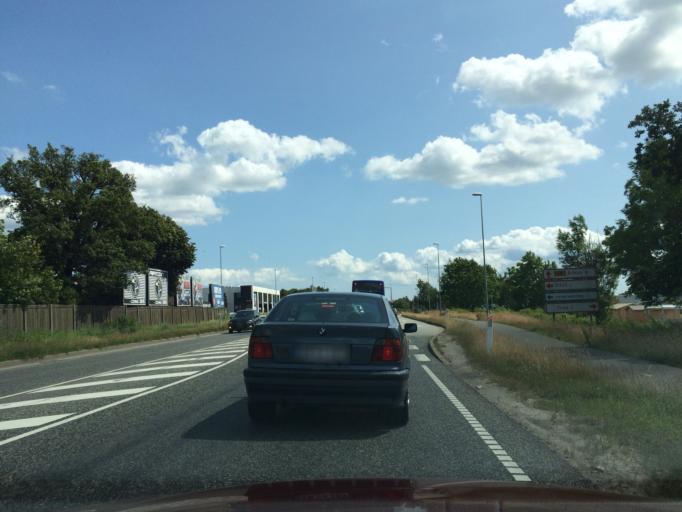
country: DK
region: Central Jutland
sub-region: Favrskov Kommune
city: Soften
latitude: 56.1846
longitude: 10.1012
